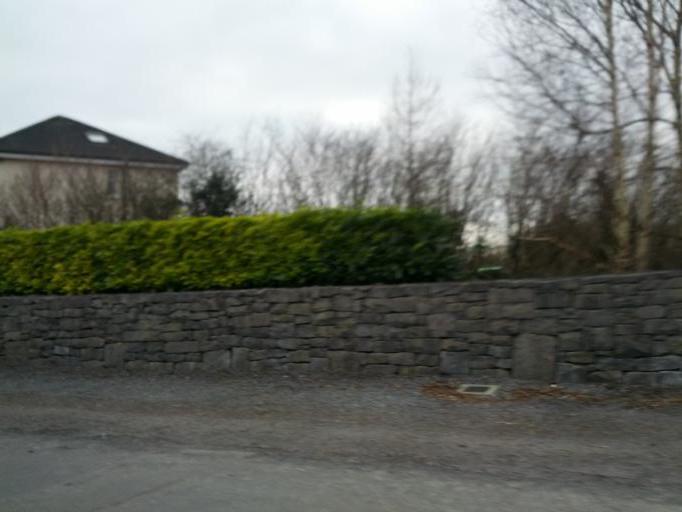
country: IE
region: Connaught
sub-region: County Galway
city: Oranmore
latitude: 53.2233
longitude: -8.8836
